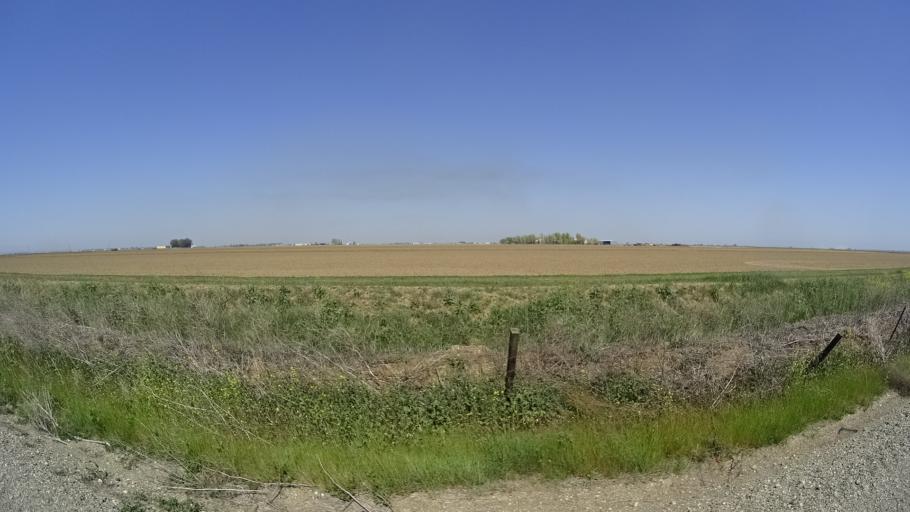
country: US
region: California
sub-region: Glenn County
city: Willows
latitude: 39.4647
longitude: -122.1314
